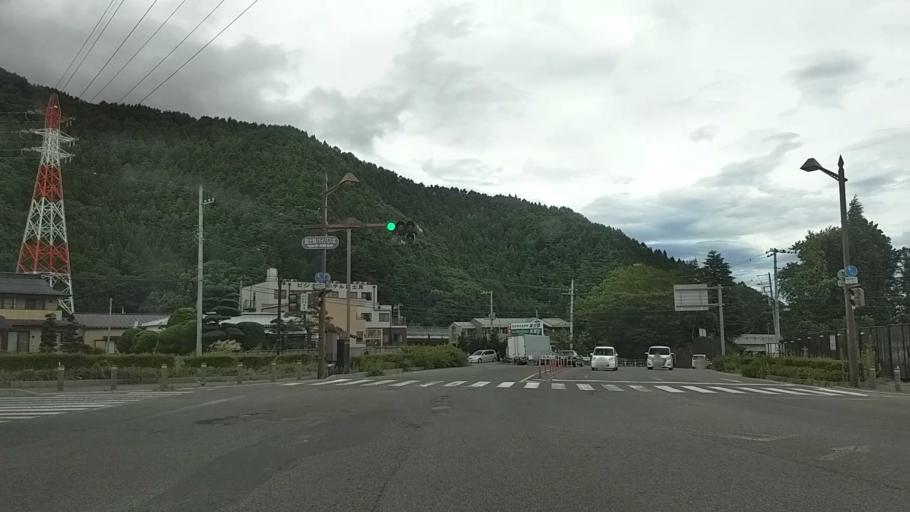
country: JP
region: Yamanashi
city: Fujikawaguchiko
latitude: 35.5033
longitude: 138.8189
